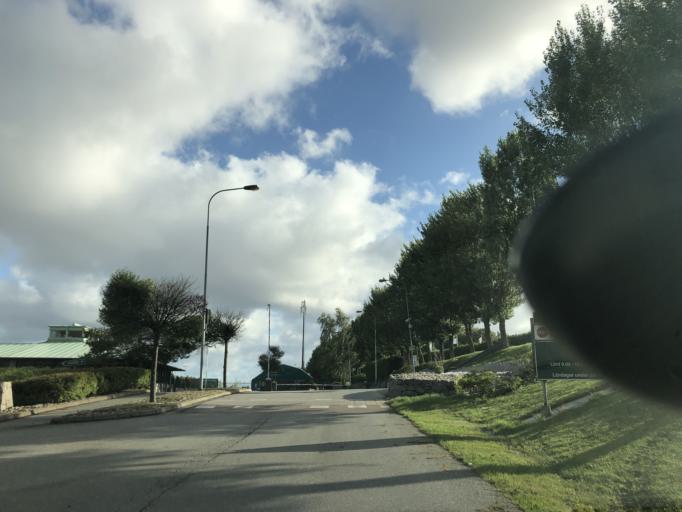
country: SE
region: Vaestra Goetaland
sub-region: Goteborg
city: Goeteborg
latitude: 57.7413
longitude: 11.9460
